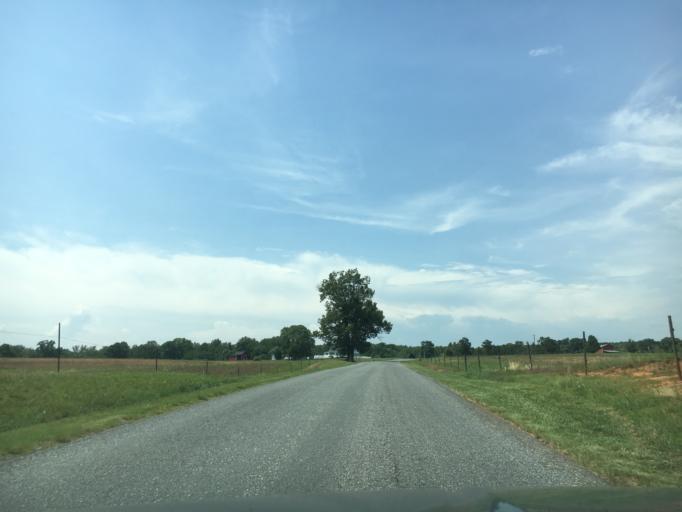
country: US
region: Virginia
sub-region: Pittsylvania County
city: Gretna
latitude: 36.9436
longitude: -79.4414
